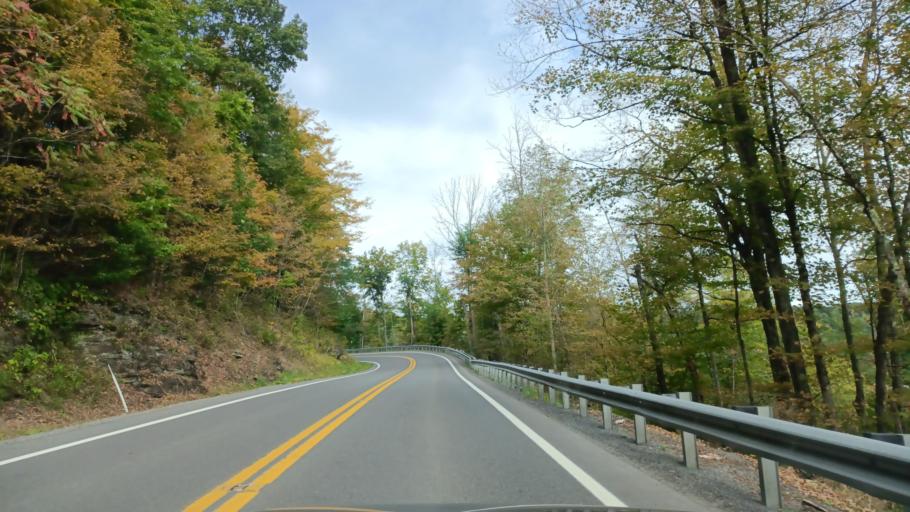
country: US
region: Maryland
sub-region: Garrett County
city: Mountain Lake Park
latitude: 39.2793
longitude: -79.3159
